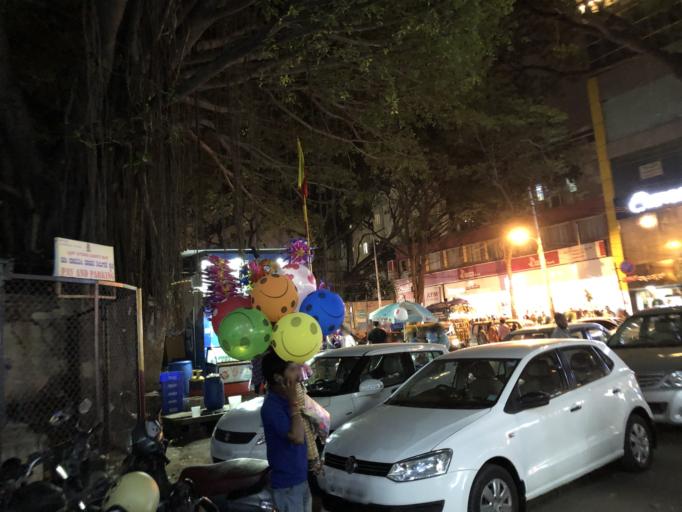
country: IN
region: Karnataka
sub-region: Bangalore Urban
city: Bangalore
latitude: 12.9299
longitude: 77.5849
